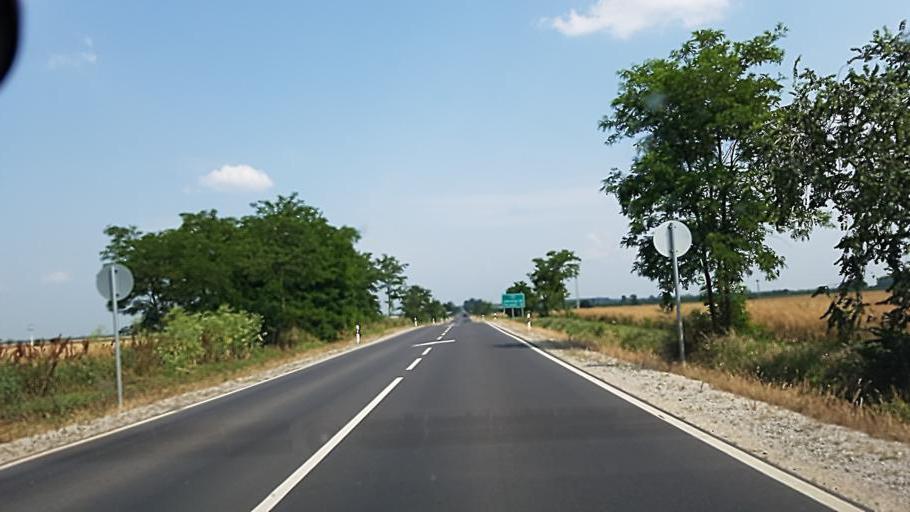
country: HU
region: Heves
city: Besenyotelek
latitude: 47.6859
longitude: 20.4756
